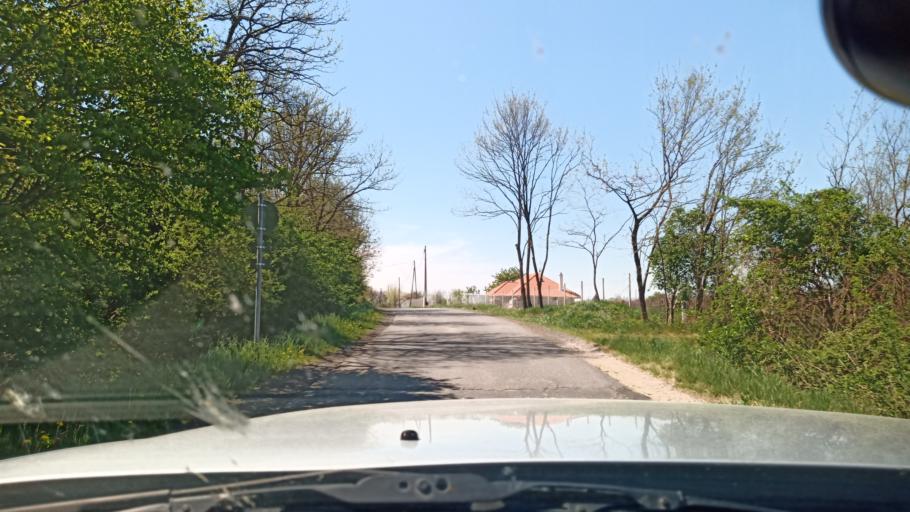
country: HU
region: Zala
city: Heviz
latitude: 46.7670
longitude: 17.1489
